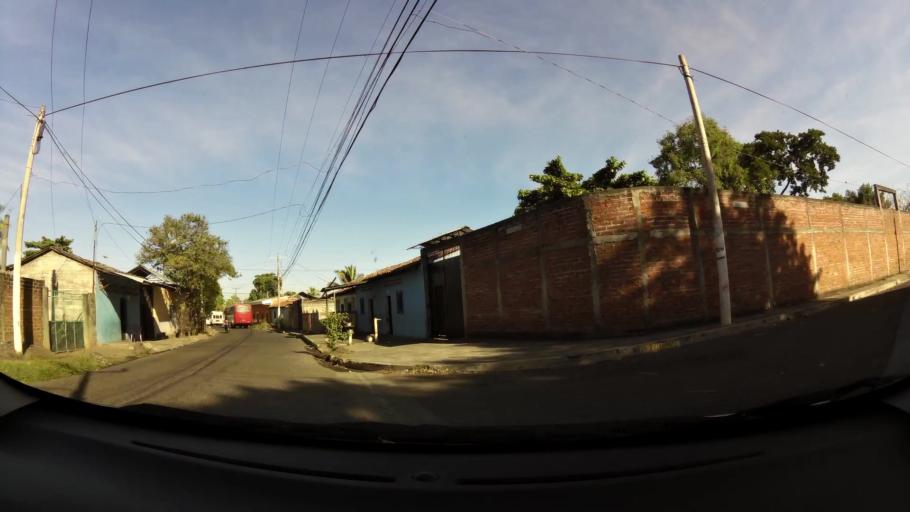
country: SV
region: San Miguel
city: San Miguel
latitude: 13.4691
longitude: -88.1894
